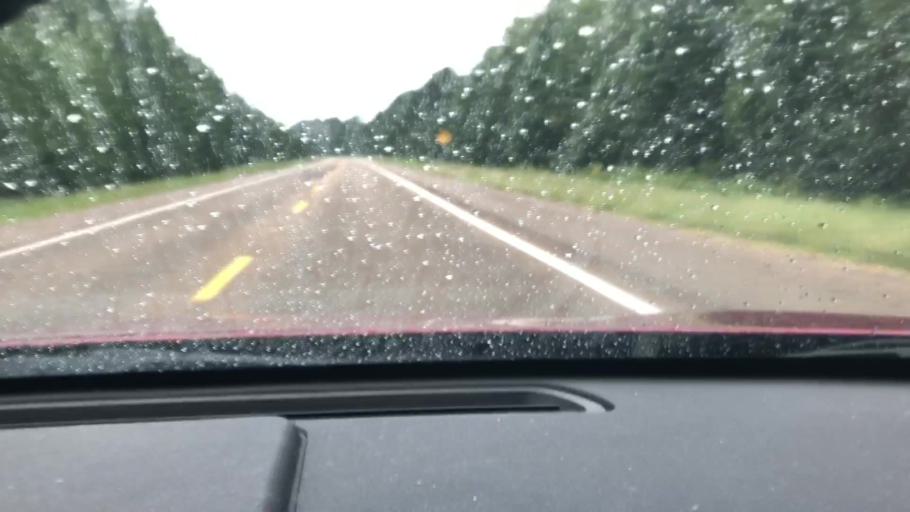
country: US
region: Arkansas
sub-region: Columbia County
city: Magnolia
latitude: 33.3015
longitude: -93.2678
